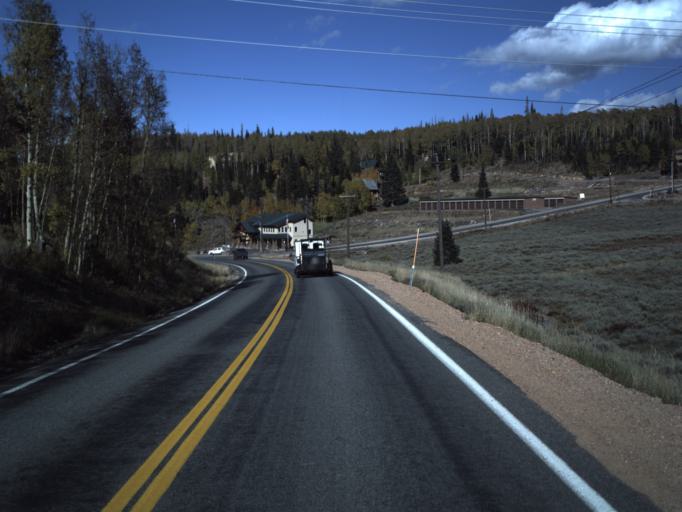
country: US
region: Utah
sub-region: Iron County
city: Parowan
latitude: 37.6965
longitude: -112.8461
